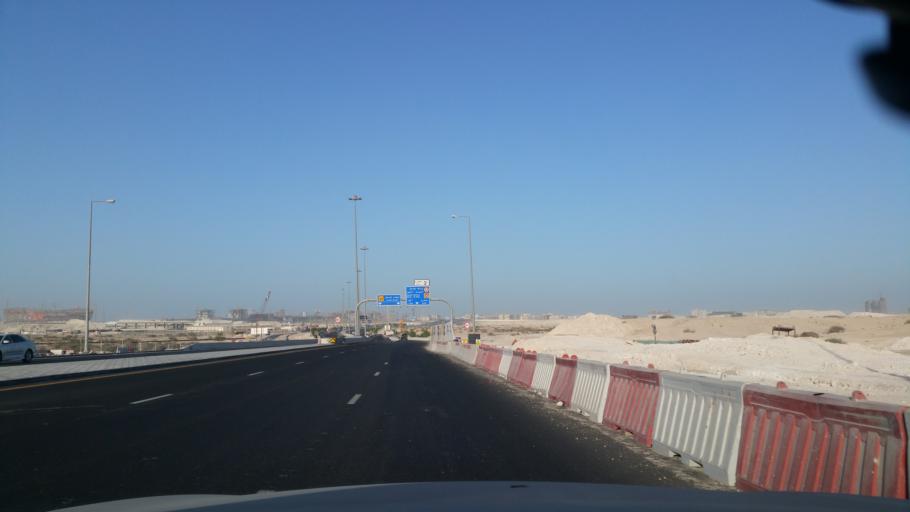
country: QA
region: Baladiyat Umm Salal
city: Umm Salal Muhammad
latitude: 25.3948
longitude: 51.4752
